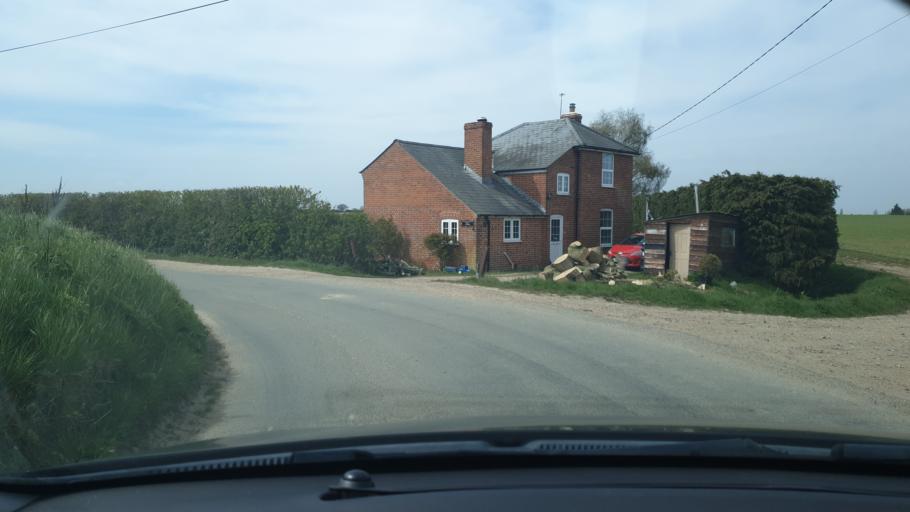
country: GB
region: England
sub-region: Essex
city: Little Clacton
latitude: 51.8996
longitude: 1.1661
